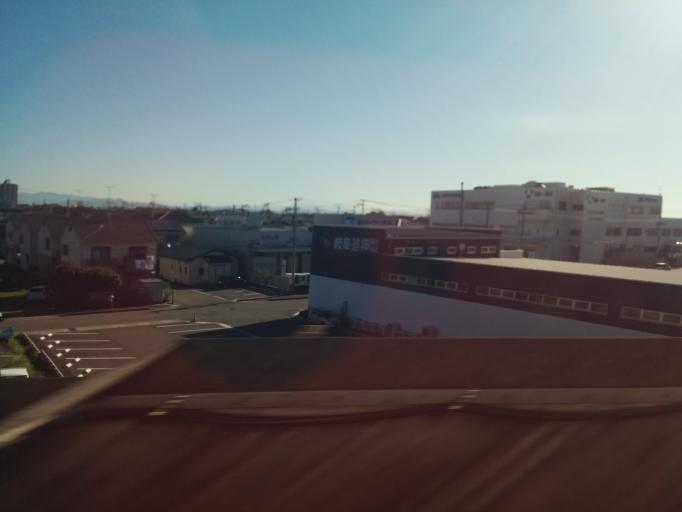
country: JP
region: Aichi
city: Sobue
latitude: 35.3096
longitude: 136.6930
